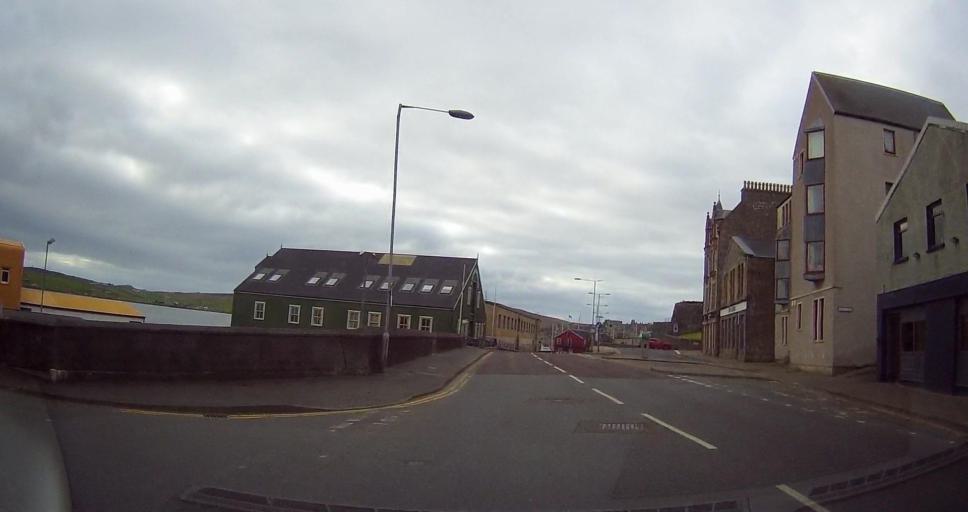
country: GB
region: Scotland
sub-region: Shetland Islands
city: Shetland
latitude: 60.1572
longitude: -1.1455
